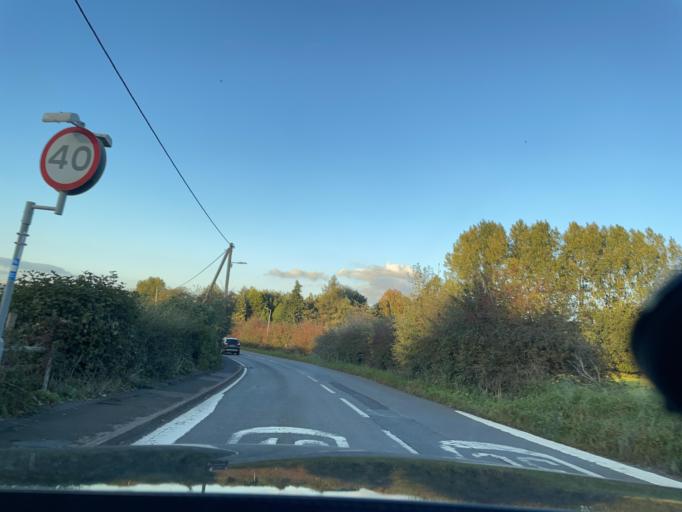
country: GB
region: England
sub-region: Borough of Tameside
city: Longdendale
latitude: 53.4360
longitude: -1.9894
